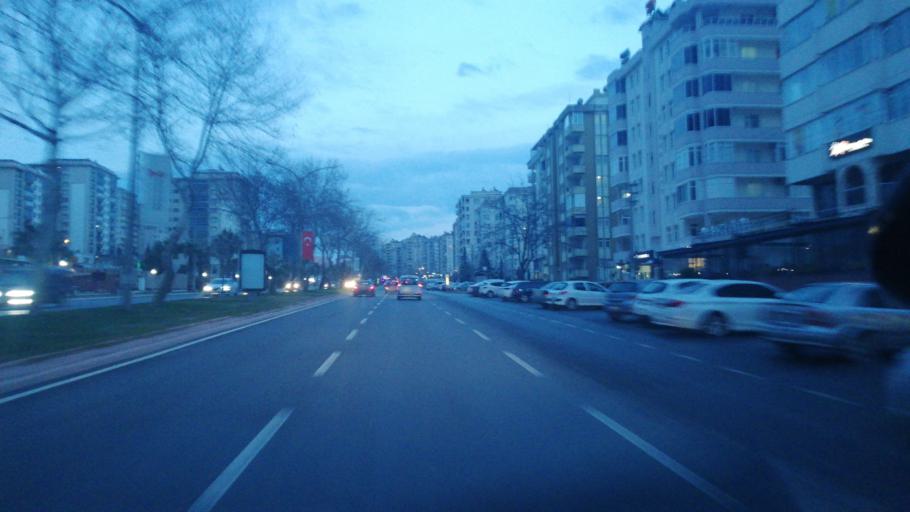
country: TR
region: Kahramanmaras
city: Kahramanmaras
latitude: 37.5903
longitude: 36.8729
